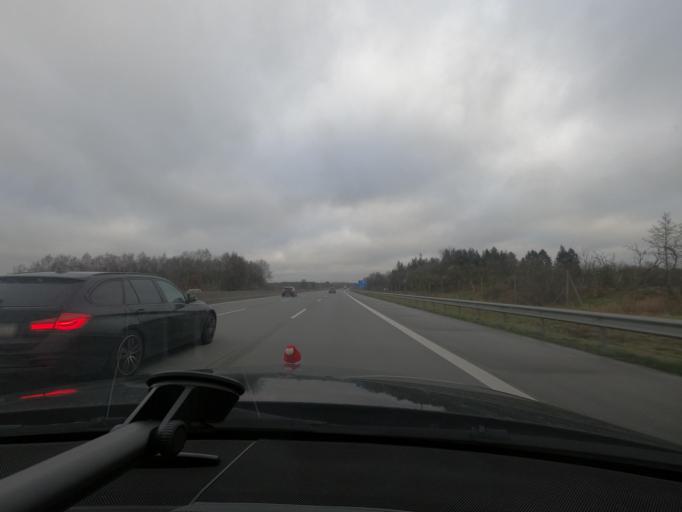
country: DE
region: Schleswig-Holstein
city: Bimohlen
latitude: 53.9109
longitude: 9.9368
